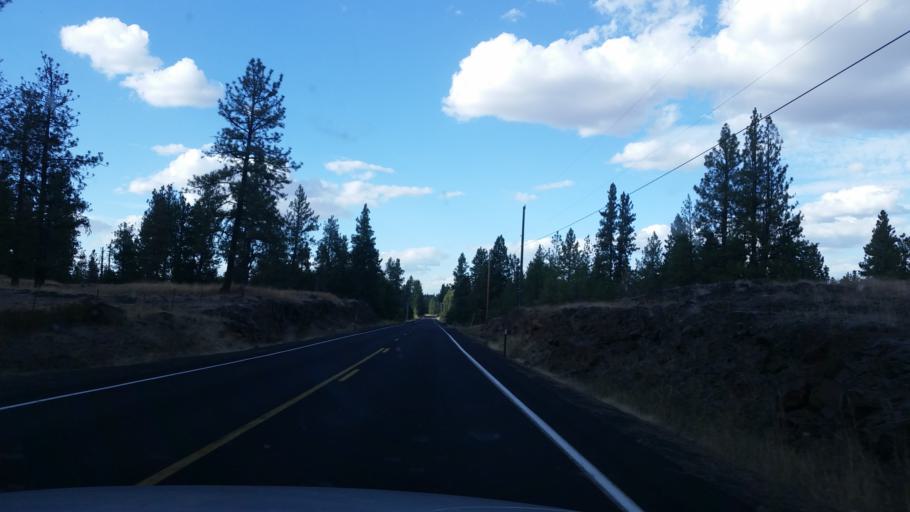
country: US
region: Washington
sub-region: Spokane County
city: Cheney
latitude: 47.4675
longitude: -117.5813
